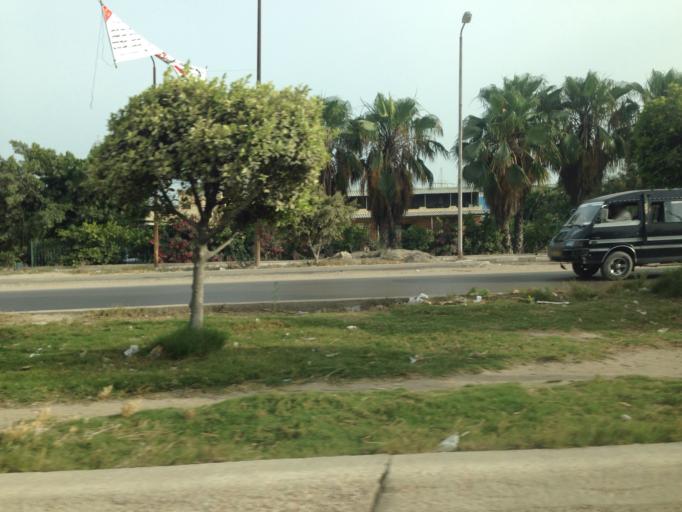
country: EG
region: Alexandria
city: Alexandria
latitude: 31.2037
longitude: 29.9978
